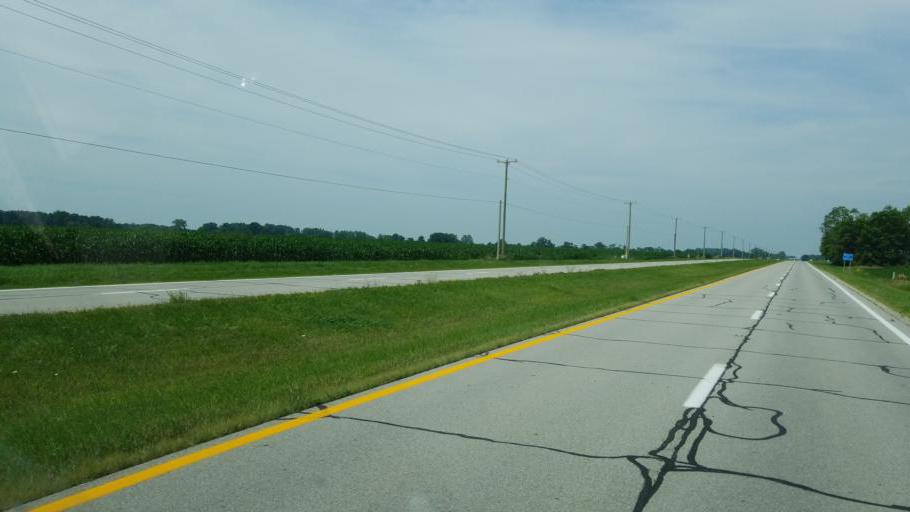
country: US
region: Ohio
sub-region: Madison County
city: London
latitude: 39.9397
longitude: -83.3668
